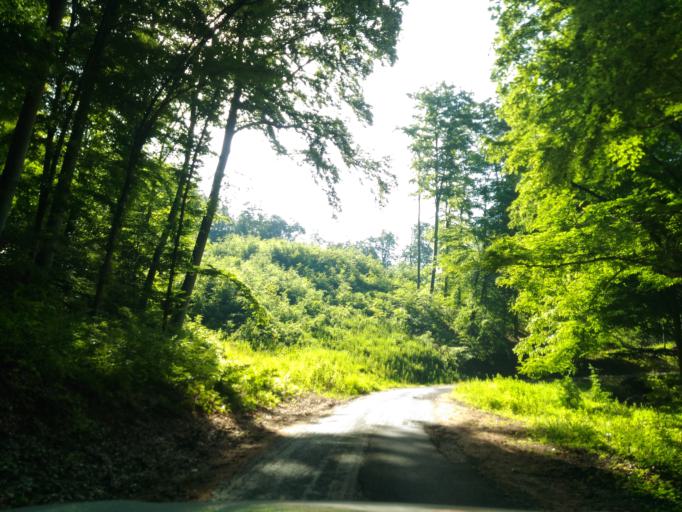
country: HU
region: Baranya
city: Hosszuheteny
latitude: 46.2237
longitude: 18.3386
